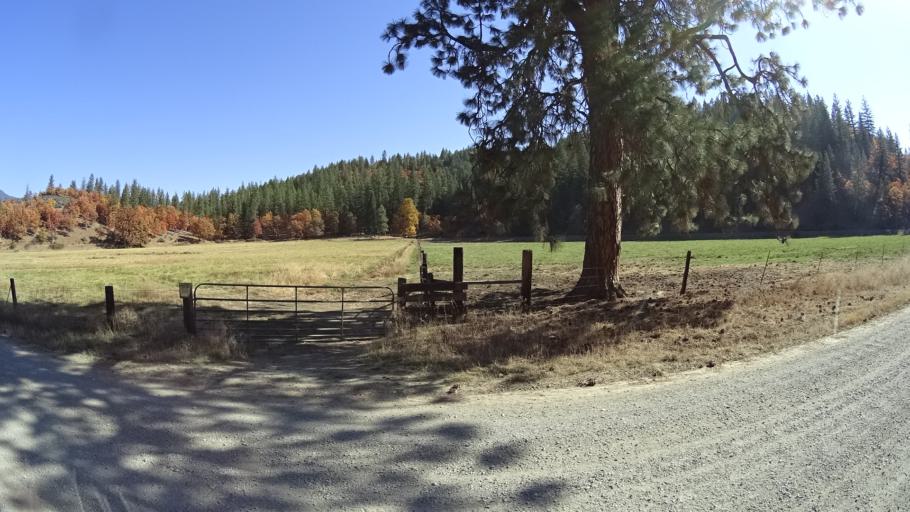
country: US
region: California
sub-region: Siskiyou County
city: Yreka
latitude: 41.6212
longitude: -122.9654
